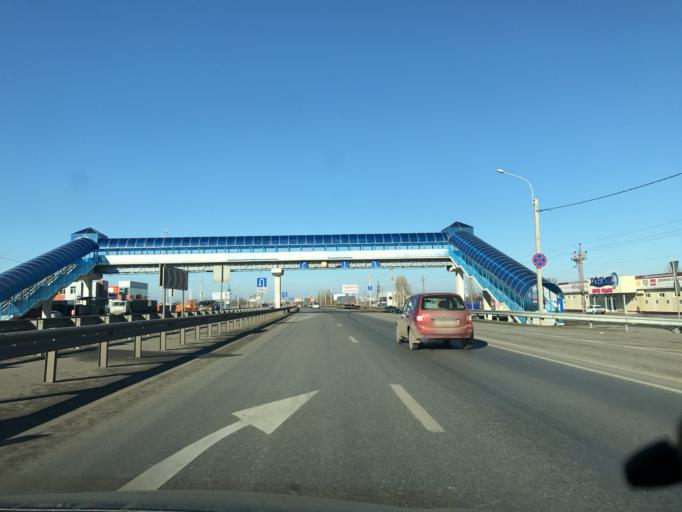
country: RU
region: Rostov
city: Bataysk
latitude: 47.1542
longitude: 39.7704
